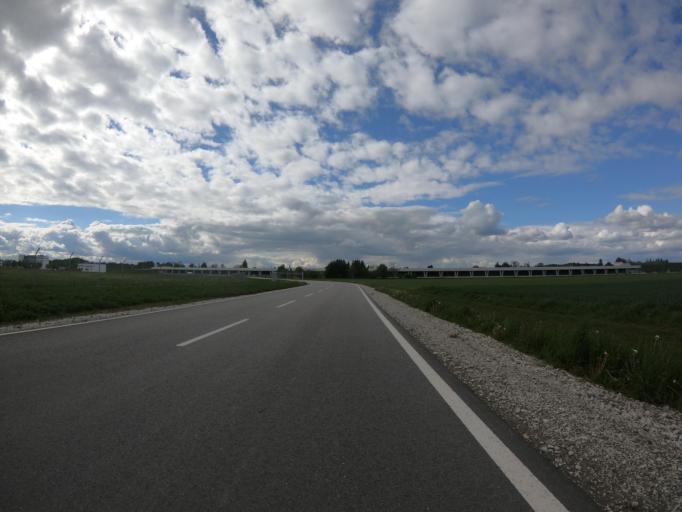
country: DE
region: Bavaria
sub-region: Upper Bavaria
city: Gilching
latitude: 48.0915
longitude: 11.2979
